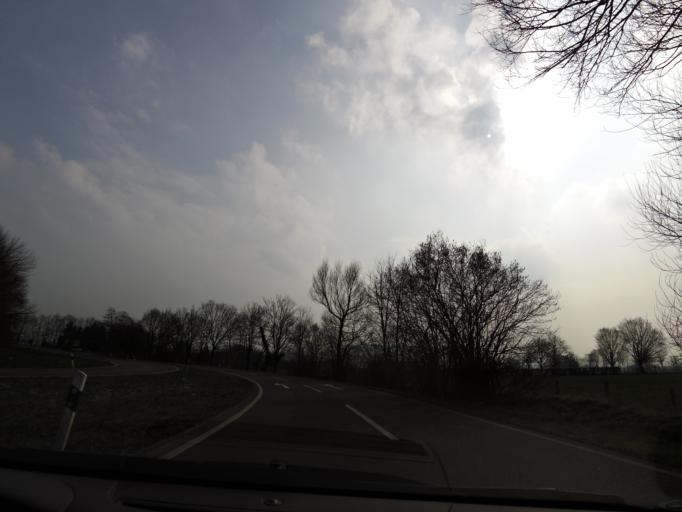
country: DE
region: North Rhine-Westphalia
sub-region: Regierungsbezirk Koln
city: Aachen
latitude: 50.8036
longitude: 6.0733
